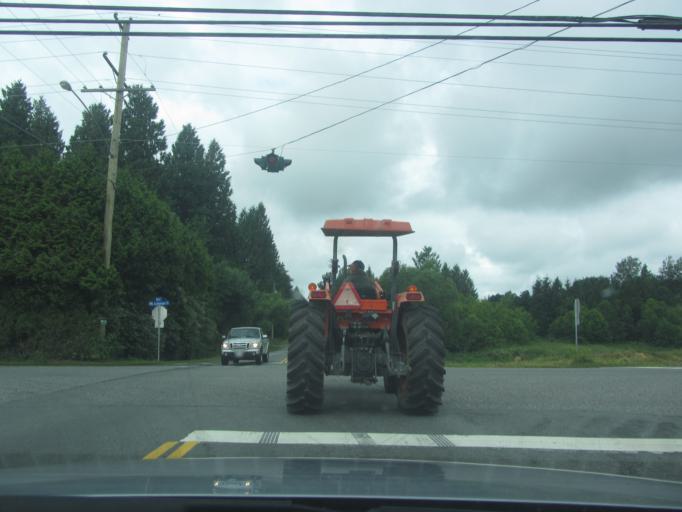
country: CA
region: British Columbia
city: Aldergrove
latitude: 49.1041
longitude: -122.3818
